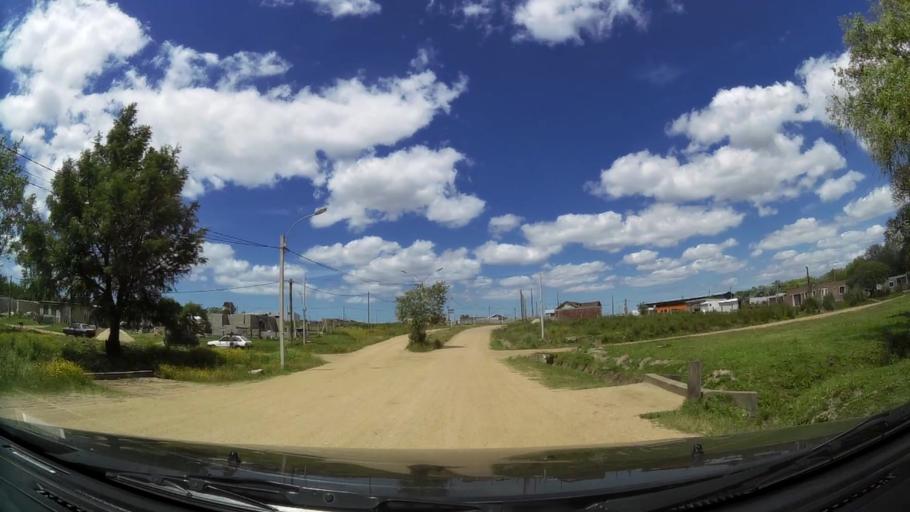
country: UY
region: Canelones
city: Colonia Nicolich
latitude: -34.8186
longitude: -56.0158
